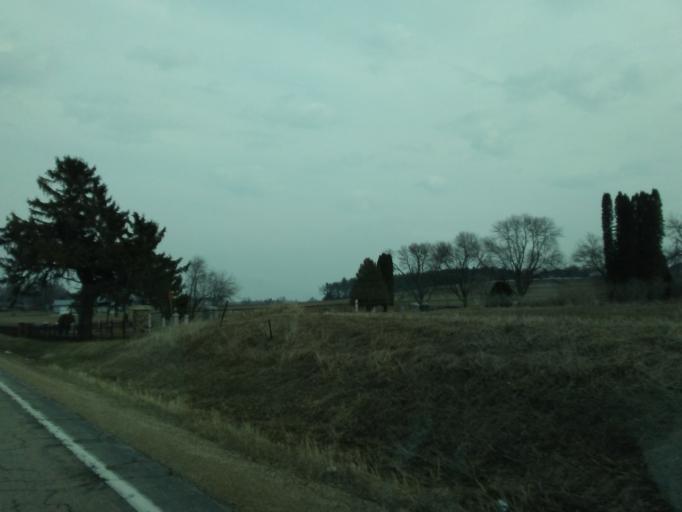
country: US
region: Wisconsin
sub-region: Dane County
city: Waunakee
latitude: 43.2173
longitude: -89.4617
